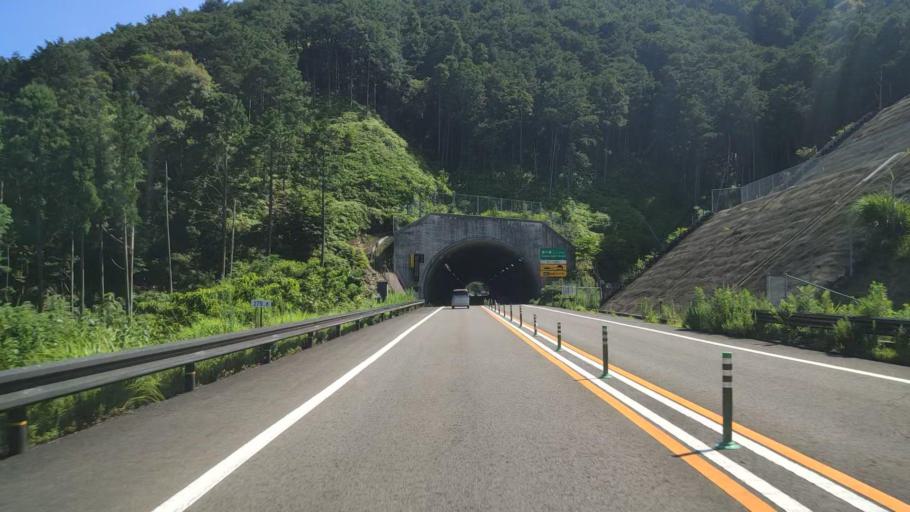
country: JP
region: Wakayama
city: Shingu
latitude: 33.6315
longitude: 135.9235
